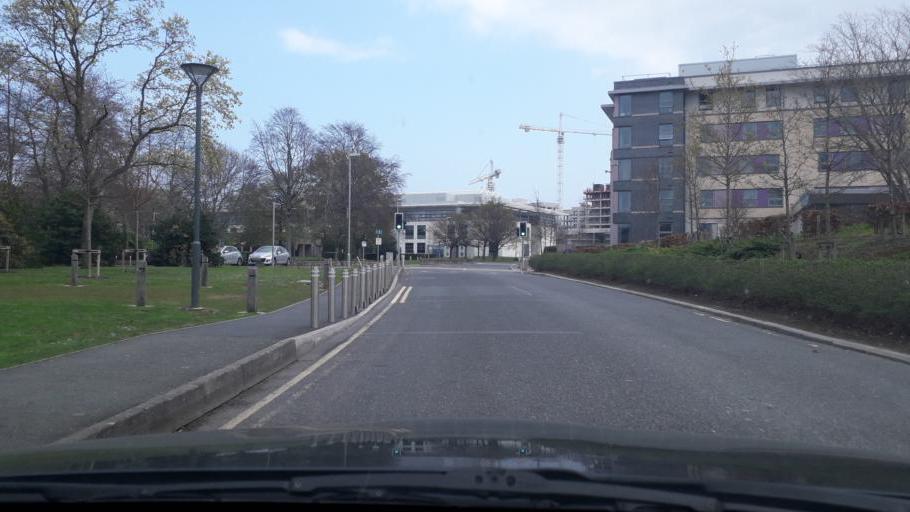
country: IE
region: Leinster
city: Donnybrook
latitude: 53.3052
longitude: -6.2228
